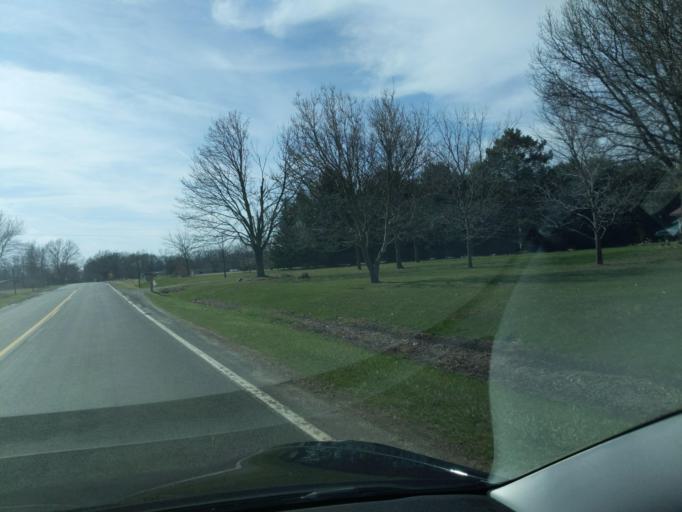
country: US
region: Michigan
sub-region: Ingham County
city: Stockbridge
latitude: 42.4832
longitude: -84.2536
